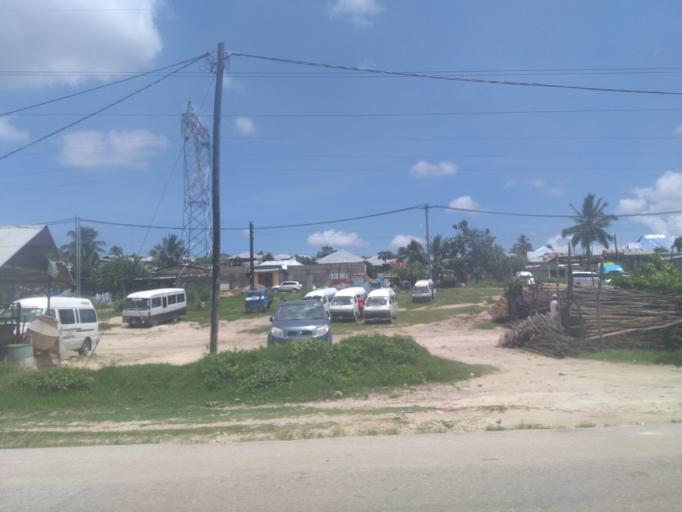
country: TZ
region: Zanzibar Urban/West
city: Zanzibar
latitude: -6.1514
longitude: 39.2216
